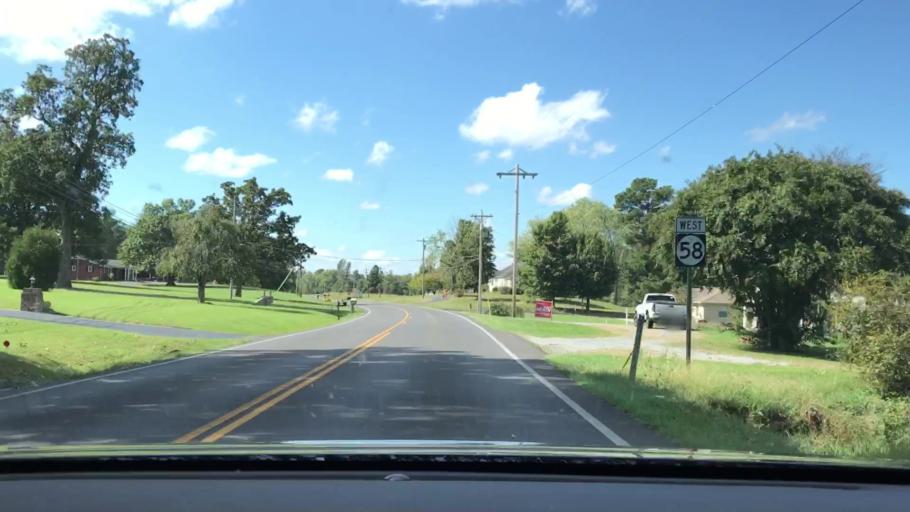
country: US
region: Kentucky
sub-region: Graves County
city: Mayfield
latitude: 36.7594
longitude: -88.5969
